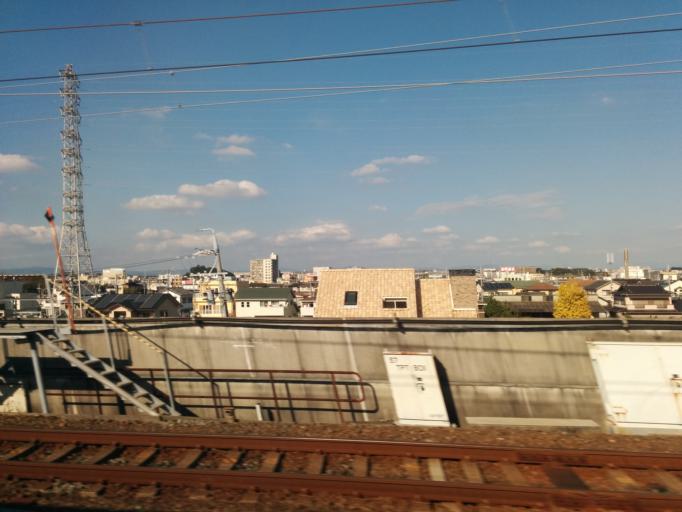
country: JP
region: Shizuoka
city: Hamamatsu
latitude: 34.6931
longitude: 137.7016
